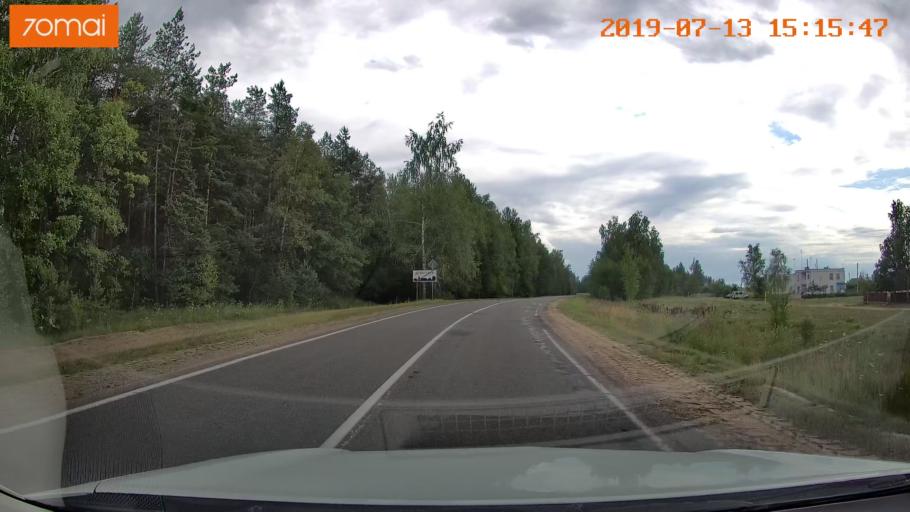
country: BY
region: Mogilev
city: Hlusha
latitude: 53.1145
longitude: 28.8288
